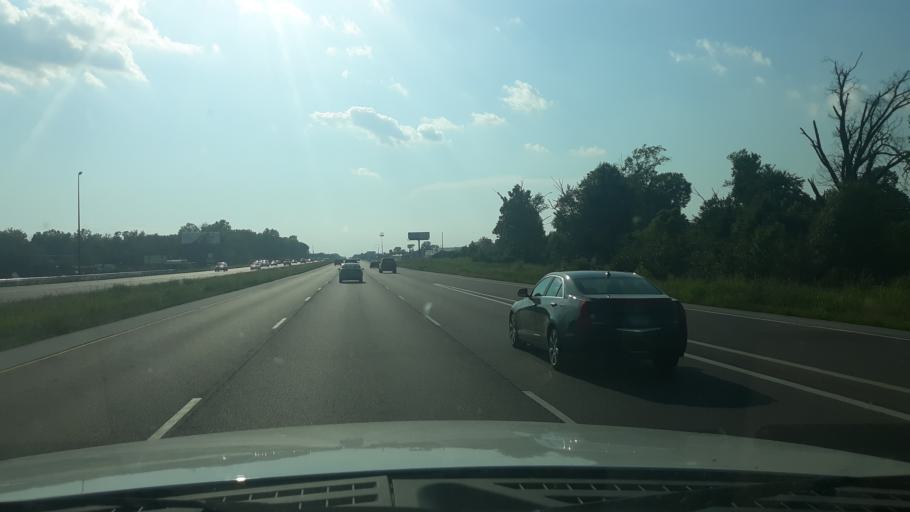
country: US
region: Illinois
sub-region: Williamson County
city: Crainville
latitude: 37.7452
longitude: -89.0631
